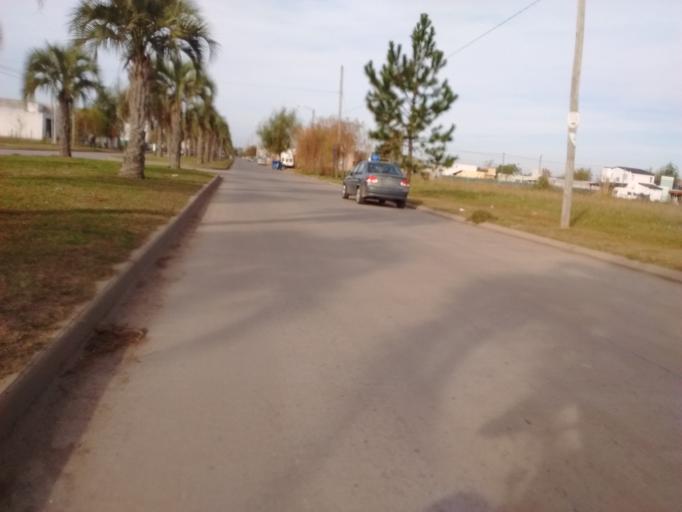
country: AR
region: Santa Fe
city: Roldan
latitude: -32.9318
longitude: -60.8962
